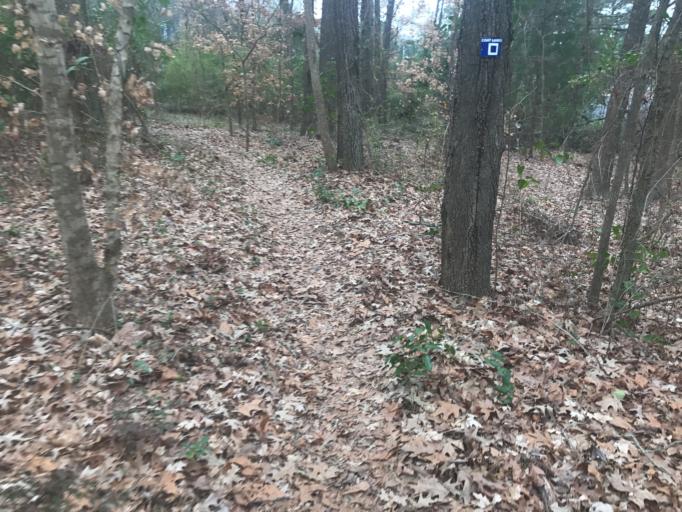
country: US
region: Texas
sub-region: Nacogdoches County
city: Nacogdoches
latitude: 31.6264
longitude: -94.6401
